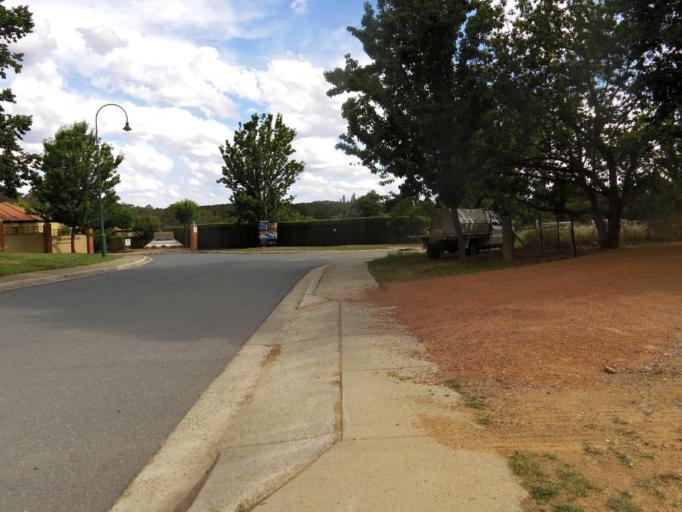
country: AU
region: Australian Capital Territory
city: Belconnen
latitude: -35.1949
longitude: 149.0896
